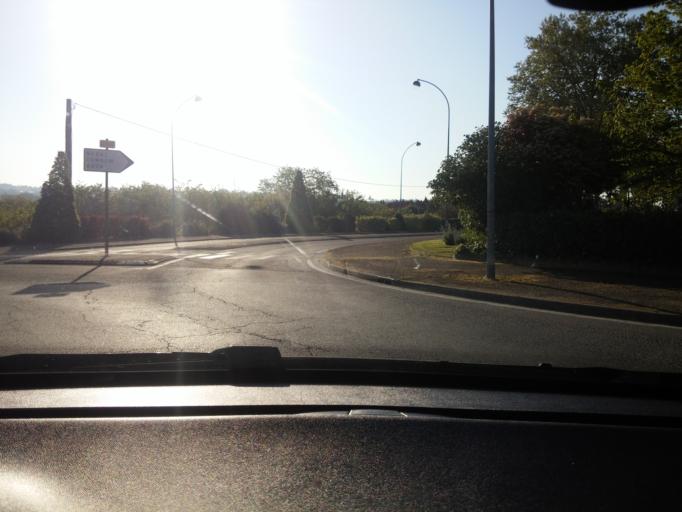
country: FR
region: Aquitaine
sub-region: Departement du Lot-et-Garonne
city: Nerac
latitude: 44.1479
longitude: 0.3256
